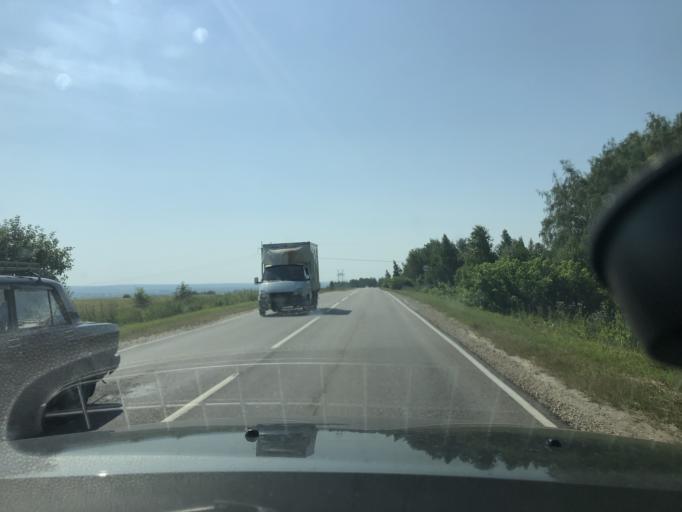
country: RU
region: Tula
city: Dubna
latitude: 54.1200
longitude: 37.0774
